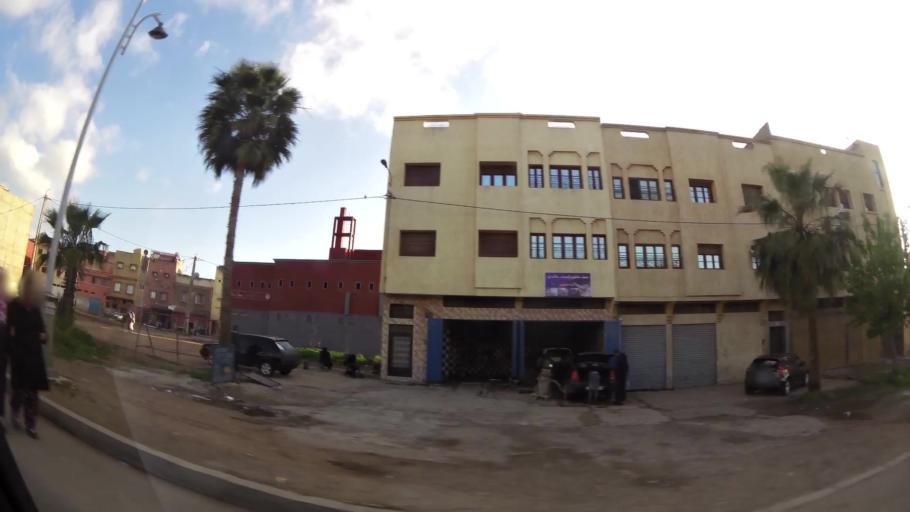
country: MA
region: Chaouia-Ouardigha
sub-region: Settat Province
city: Settat
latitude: 33.0041
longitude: -7.6083
